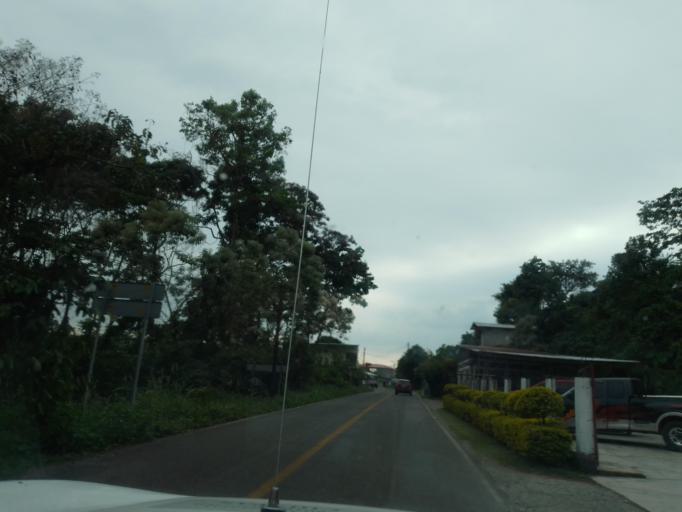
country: MX
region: Chiapas
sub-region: Union Juarez
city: Santo Domingo
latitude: 15.0434
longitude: -92.1360
